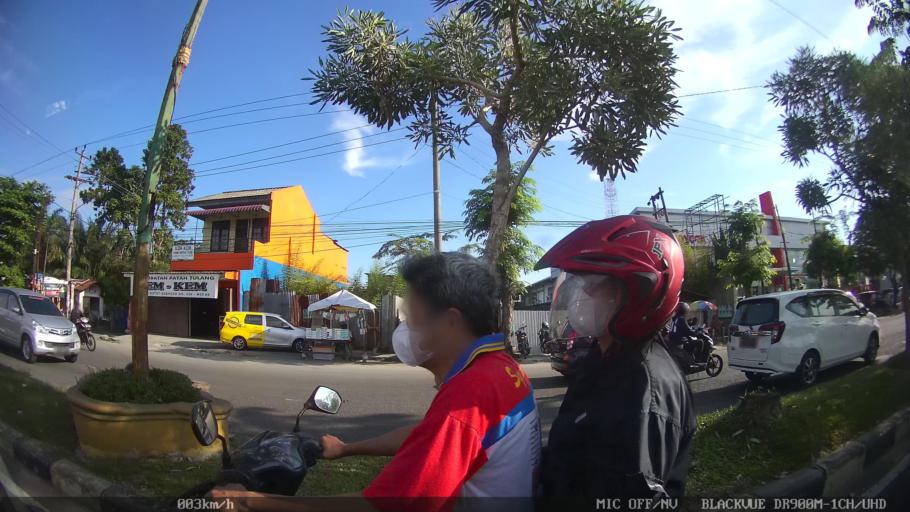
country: ID
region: North Sumatra
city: Sunggal
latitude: 3.5912
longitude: 98.6339
